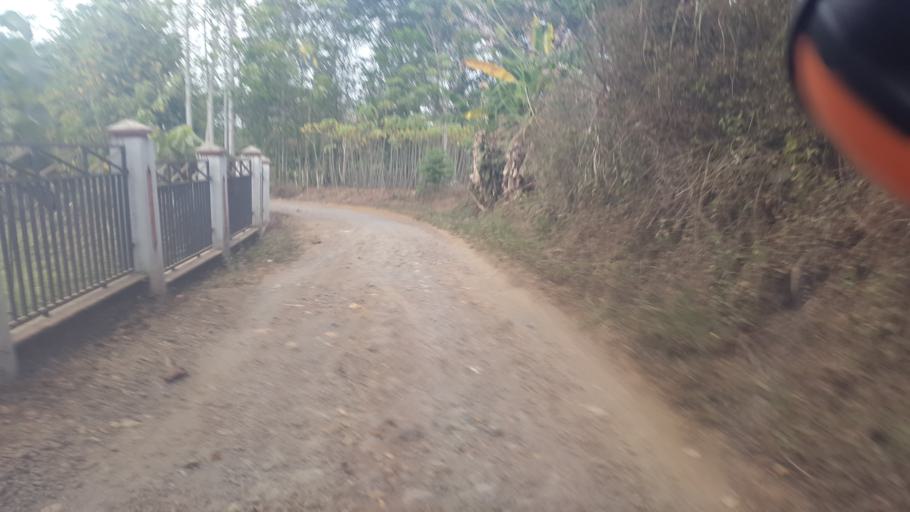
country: ID
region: West Java
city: Purabaya
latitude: -7.0944
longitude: 106.8657
